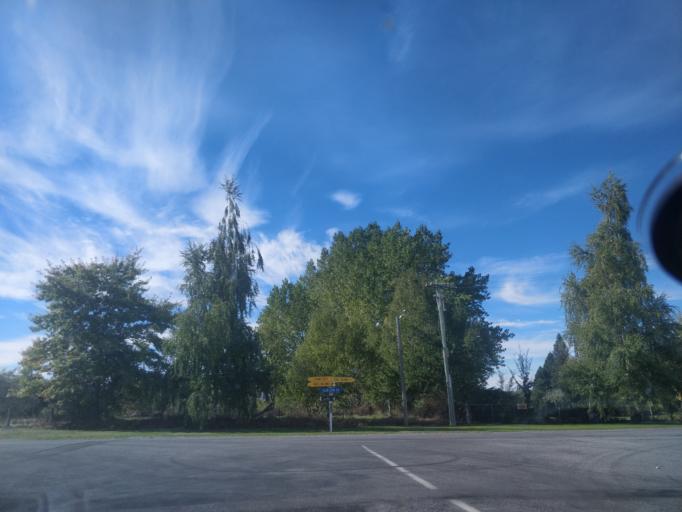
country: NZ
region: Canterbury
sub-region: Timaru District
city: Pleasant Point
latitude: -44.2530
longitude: 170.1016
